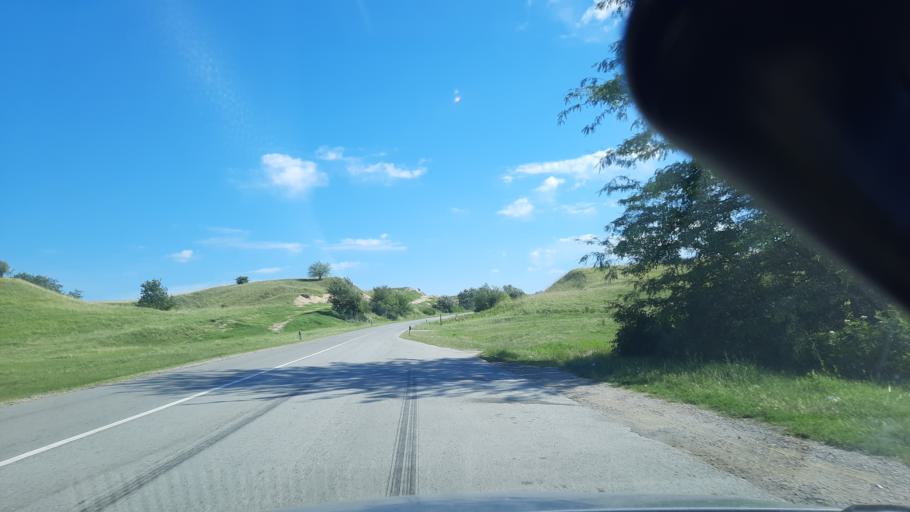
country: RO
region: Caras-Severin
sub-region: Comuna Socol
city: Socol
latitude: 44.8622
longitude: 21.3075
